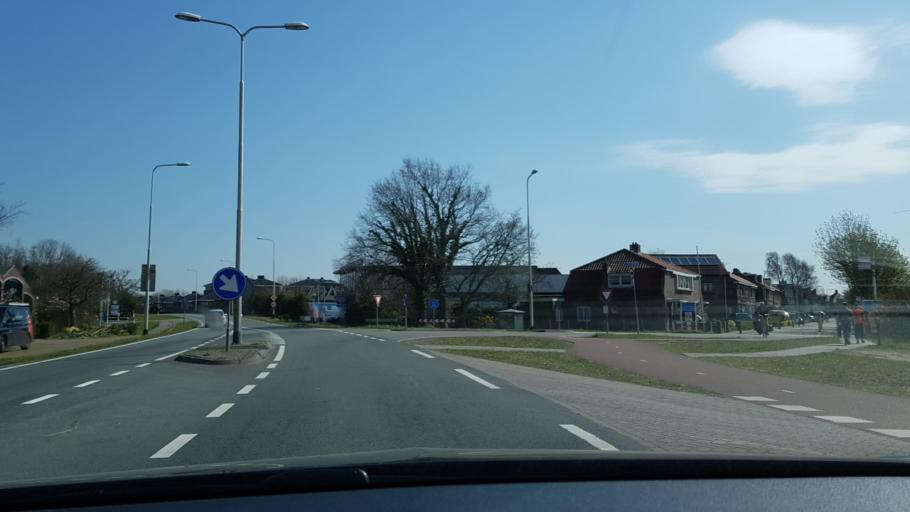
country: NL
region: South Holland
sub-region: Gemeente Teylingen
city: Sassenheim
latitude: 52.2332
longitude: 4.5191
